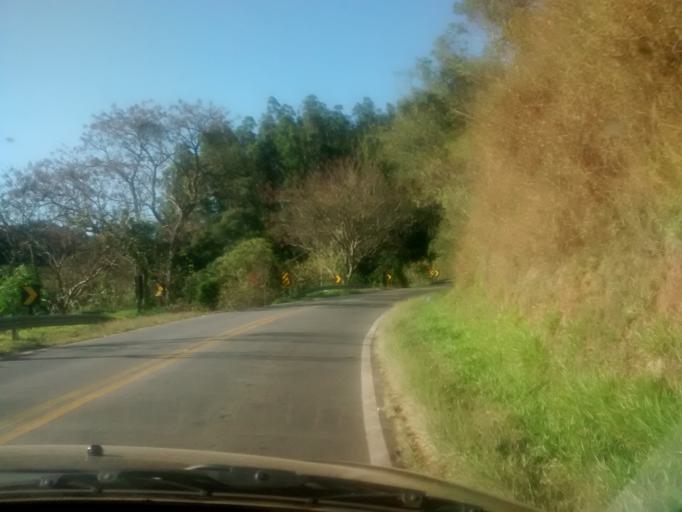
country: BR
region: Sao Paulo
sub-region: Campos Do Jordao
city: Campos do Jordao
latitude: -22.8248
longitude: -45.7349
